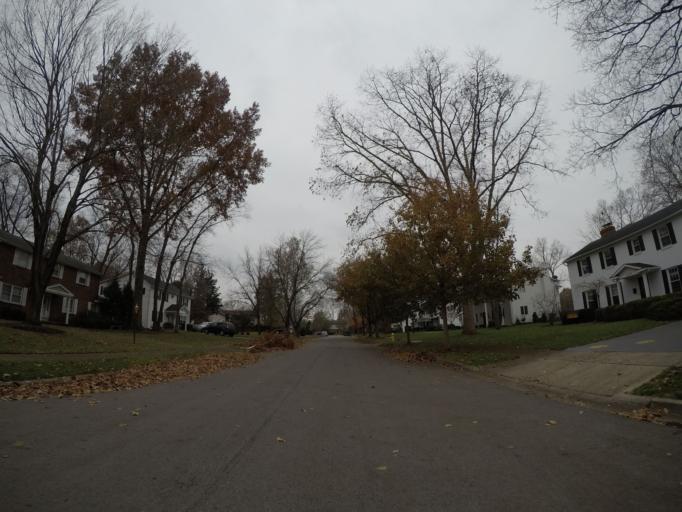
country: US
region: Ohio
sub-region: Franklin County
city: Dublin
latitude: 40.0468
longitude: -83.0936
